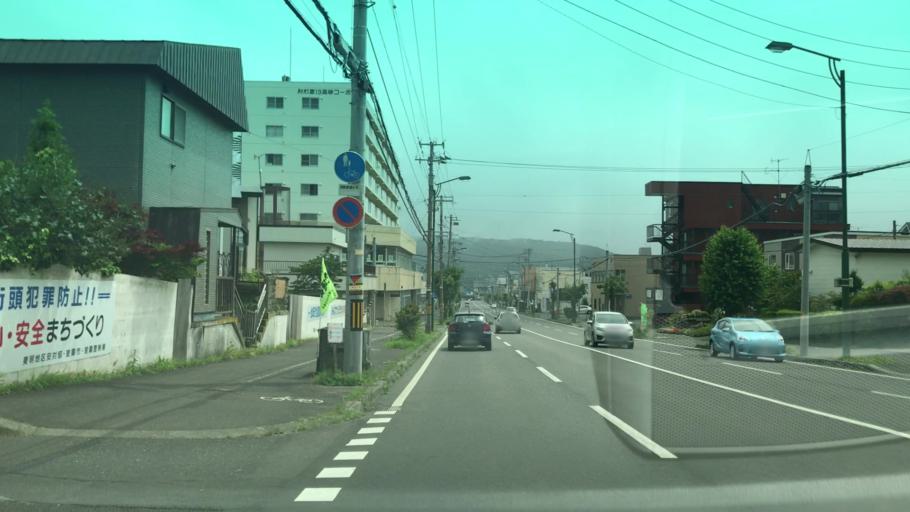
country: JP
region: Hokkaido
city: Muroran
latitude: 42.3646
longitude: 141.0373
